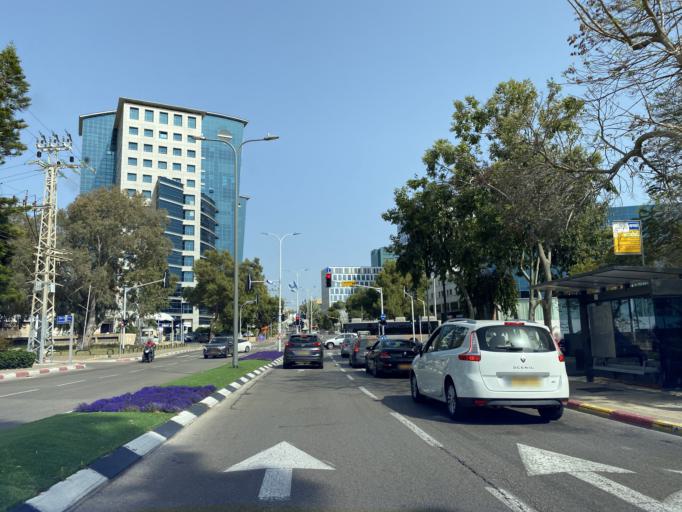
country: IL
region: Tel Aviv
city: Herzliya Pituah
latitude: 32.1669
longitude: 34.8084
